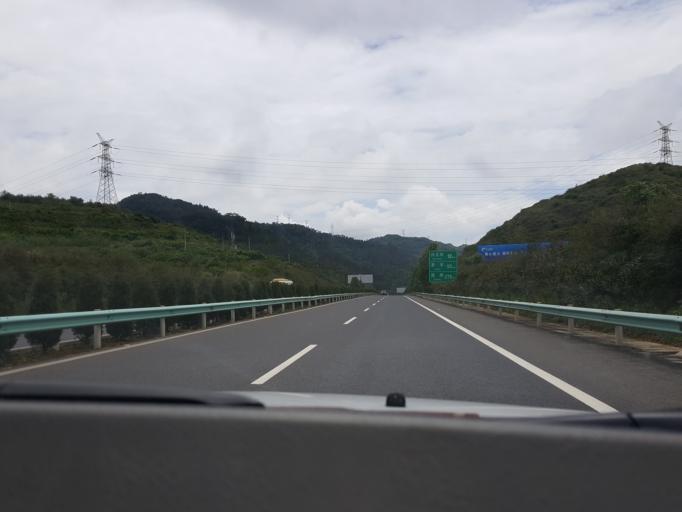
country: CN
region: Guangxi Zhuangzu Zizhiqu
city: Xinzhou
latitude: 25.1902
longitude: 105.0234
